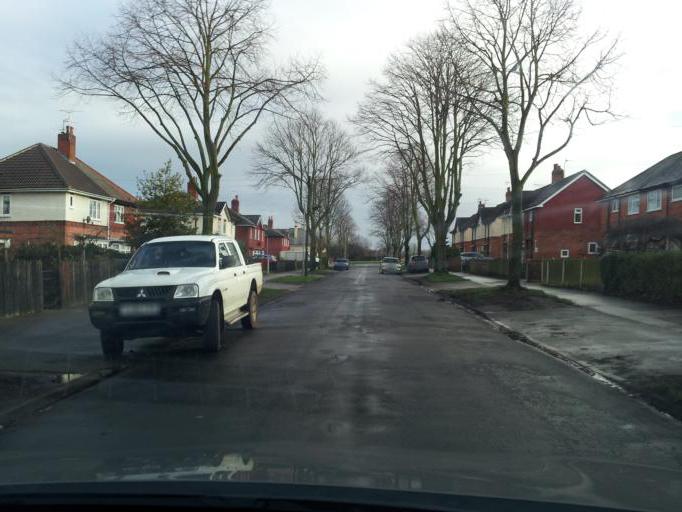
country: GB
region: England
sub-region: Nottinghamshire
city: Newark on Trent
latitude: 53.0639
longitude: -0.8066
